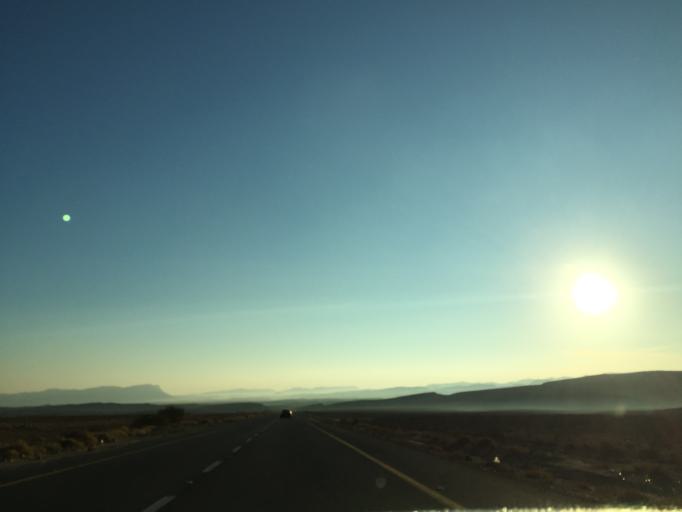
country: IL
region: Southern District
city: Mitzpe Ramon
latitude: 30.6248
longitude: 34.8296
